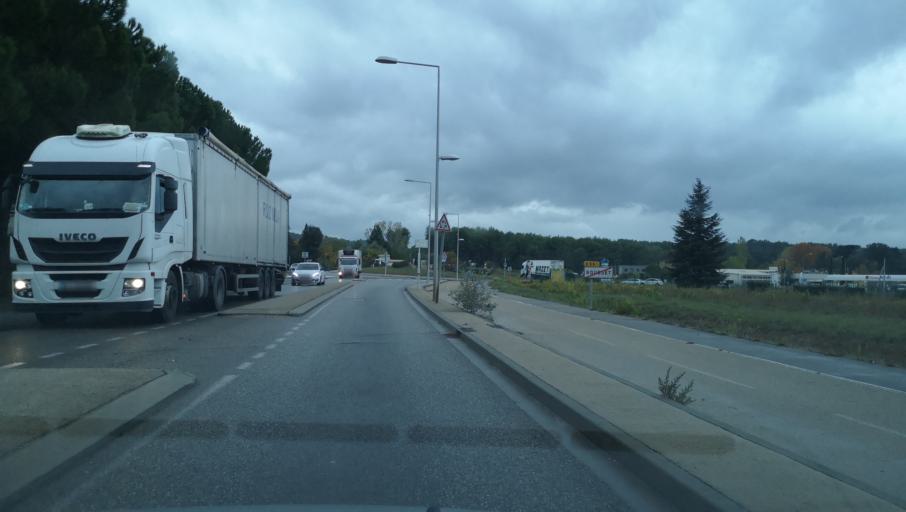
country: FR
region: Provence-Alpes-Cote d'Azur
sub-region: Departement des Bouches-du-Rhone
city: Rousset
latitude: 43.4647
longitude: 5.6116
